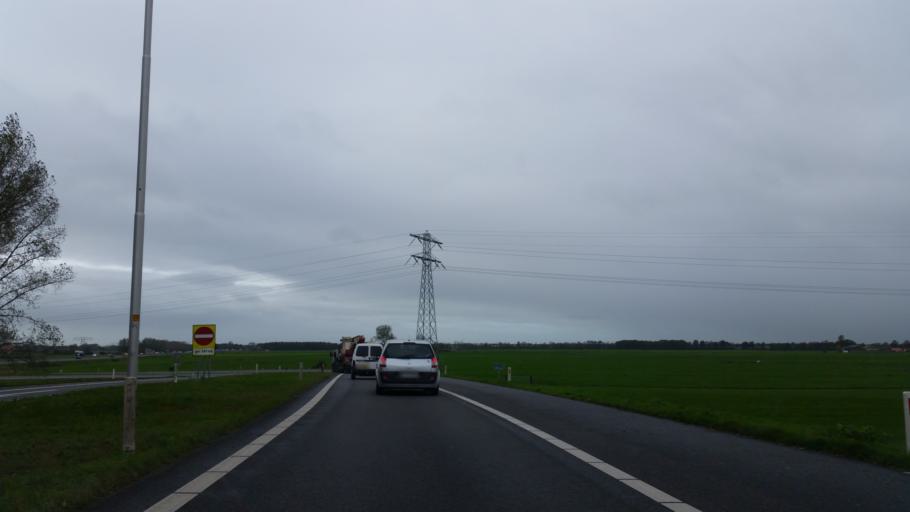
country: NL
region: Friesland
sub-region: Gemeente Skarsterlan
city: Oudehaske
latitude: 52.9649
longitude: 5.8691
